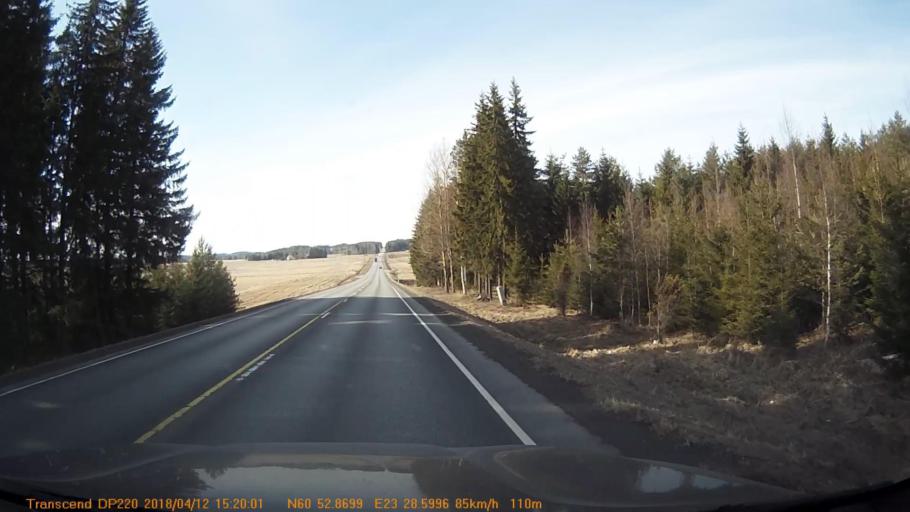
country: FI
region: Haeme
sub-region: Forssa
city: Jokioinen
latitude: 60.8814
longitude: 23.4761
